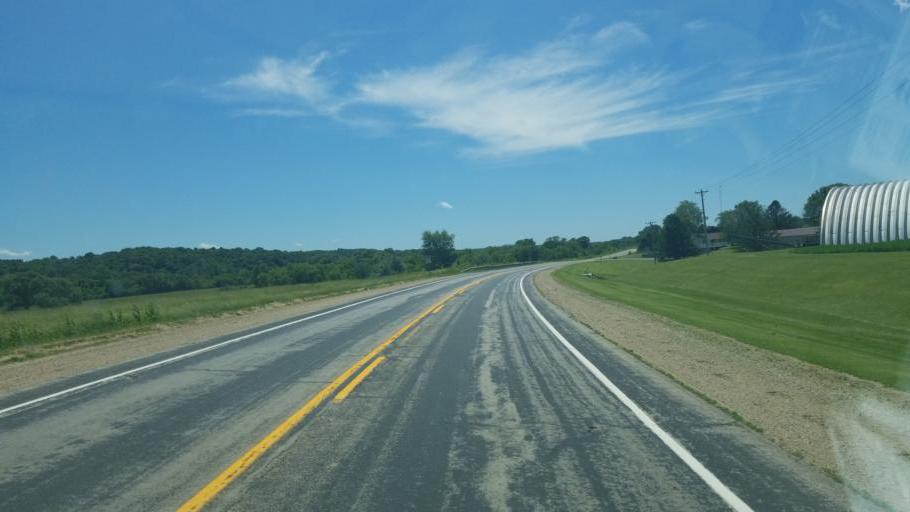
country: US
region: Wisconsin
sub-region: Vernon County
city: Hillsboro
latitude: 43.6653
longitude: -90.3198
